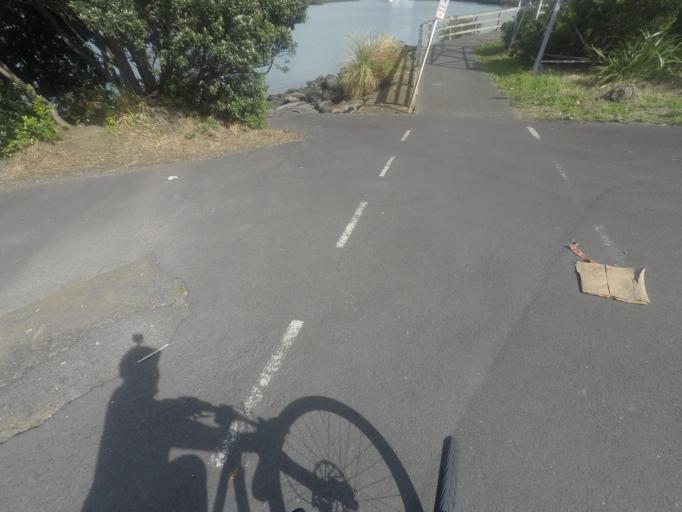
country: NZ
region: Auckland
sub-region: Auckland
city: Mangere
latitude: -36.9296
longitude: 174.7820
